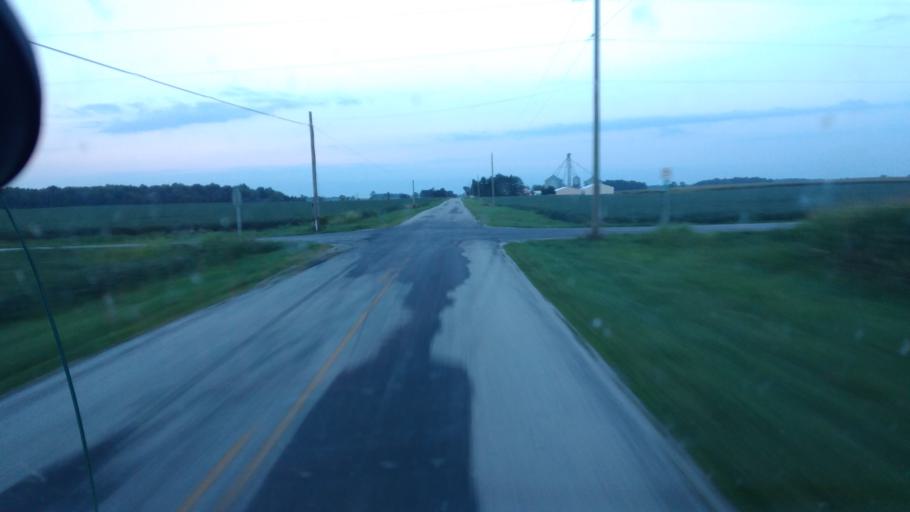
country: US
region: Ohio
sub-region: Hardin County
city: Kenton
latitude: 40.6722
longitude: -83.4961
